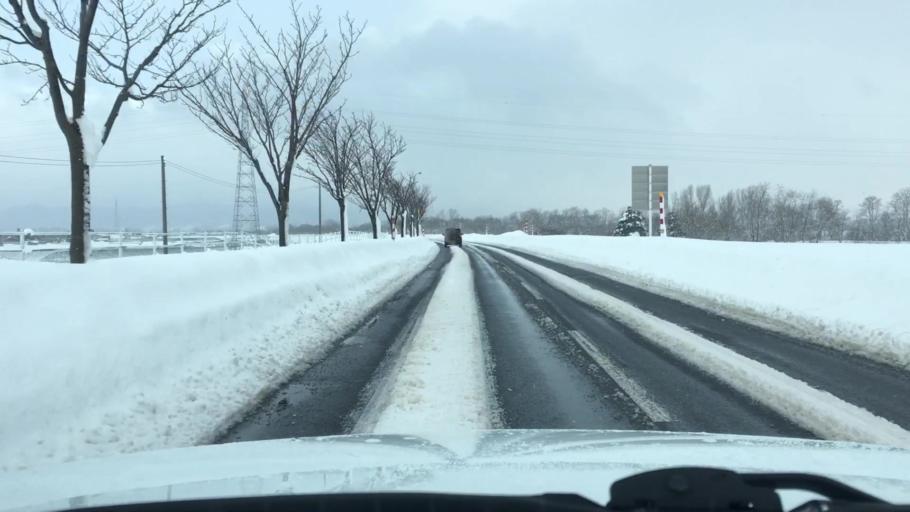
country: JP
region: Aomori
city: Hirosaki
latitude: 40.6404
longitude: 140.4720
